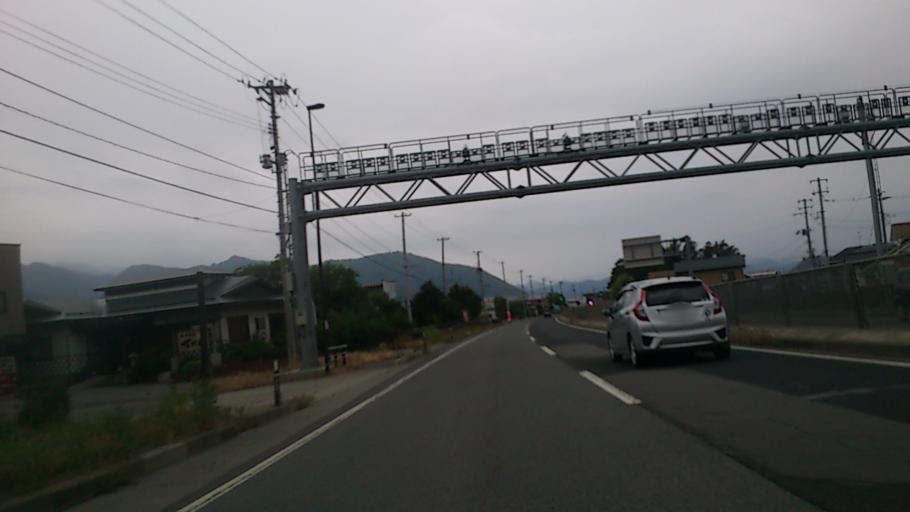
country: JP
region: Yamagata
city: Tendo
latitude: 38.3909
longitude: 140.3803
